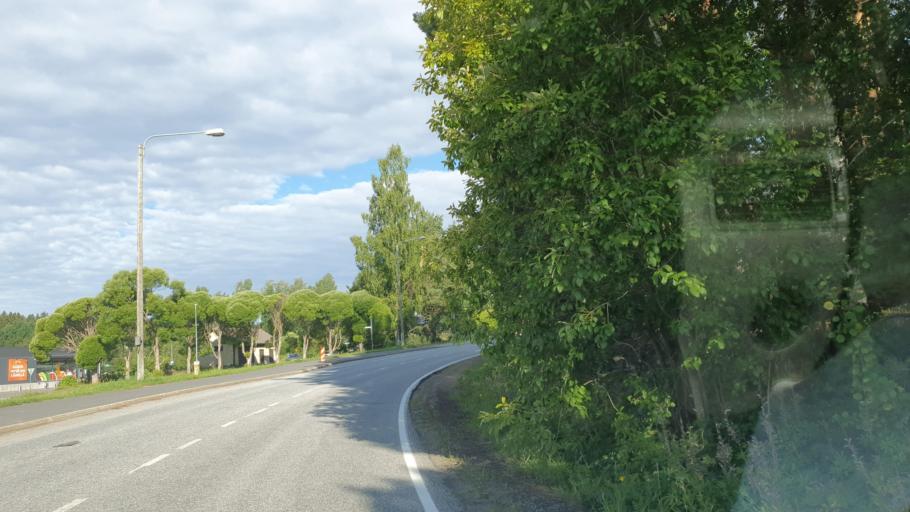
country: FI
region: Central Finland
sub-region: Jyvaeskylae
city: Saeynaetsalo
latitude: 62.1552
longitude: 25.7576
